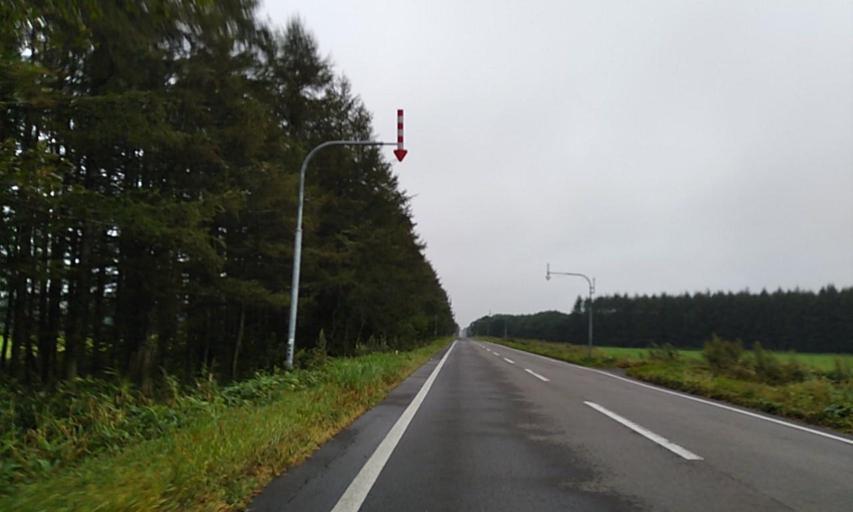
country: JP
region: Hokkaido
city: Shibetsu
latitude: 43.5223
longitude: 144.6878
